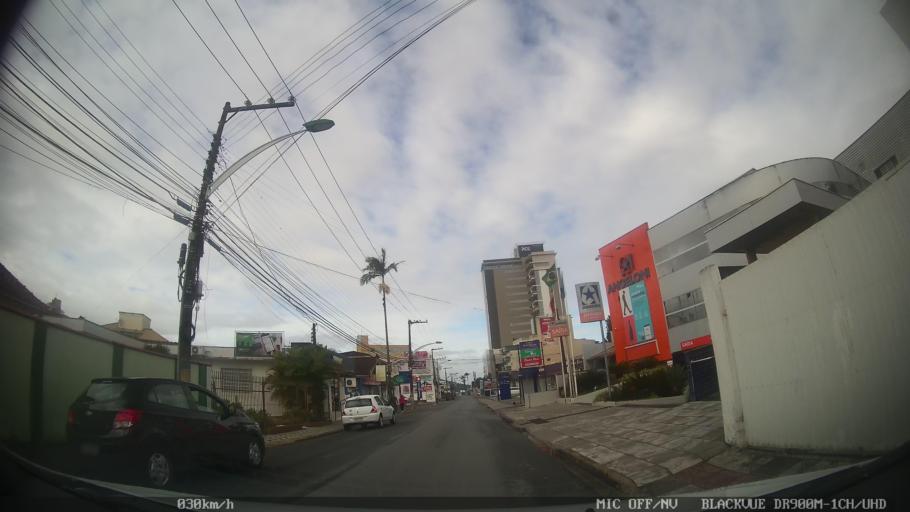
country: BR
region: Santa Catarina
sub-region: Biguacu
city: Biguacu
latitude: -27.4975
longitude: -48.6550
